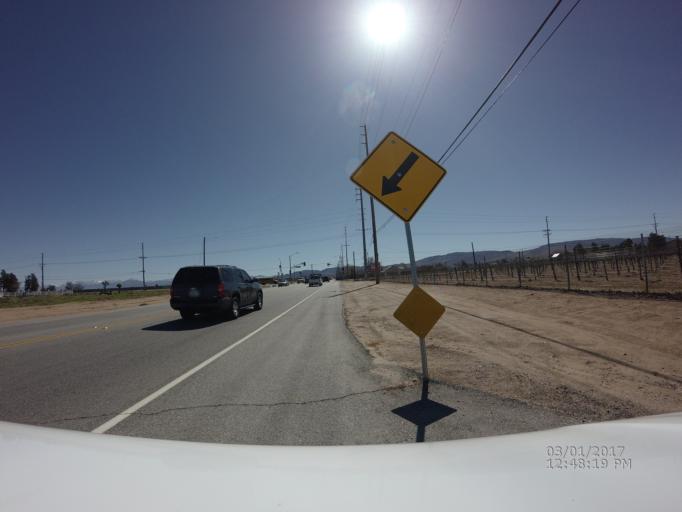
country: US
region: California
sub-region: Los Angeles County
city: Quartz Hill
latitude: 34.6467
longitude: -118.1657
